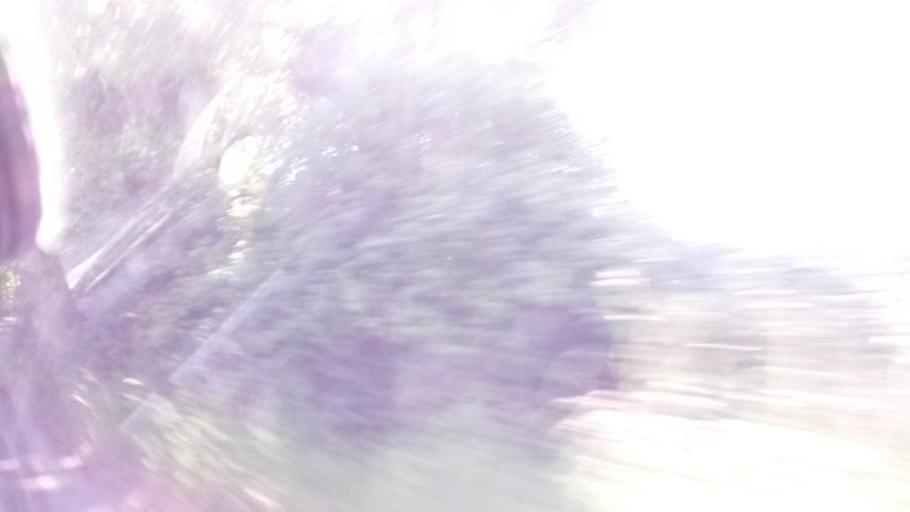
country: IE
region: Leinster
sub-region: An Mhi
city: Ashbourne
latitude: 53.5338
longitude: -6.3231
